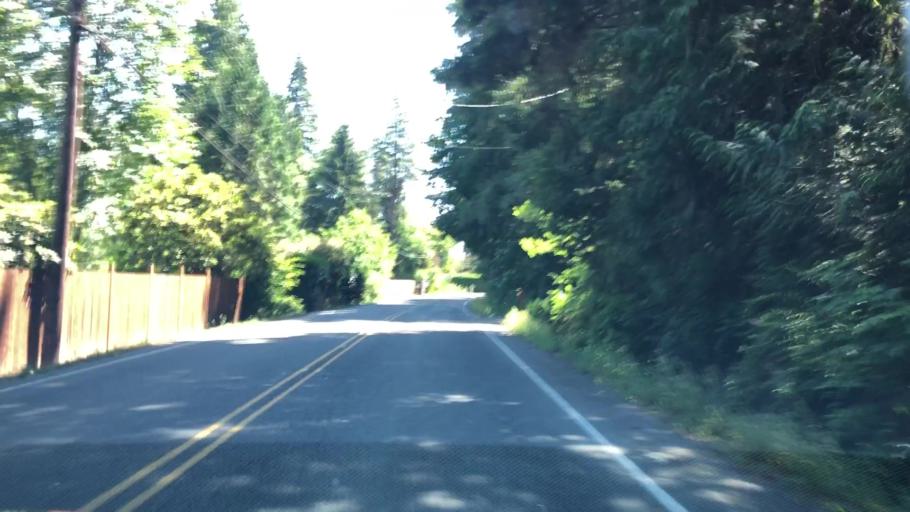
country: US
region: Washington
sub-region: King County
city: Cottage Lake
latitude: 47.7558
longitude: -122.1091
